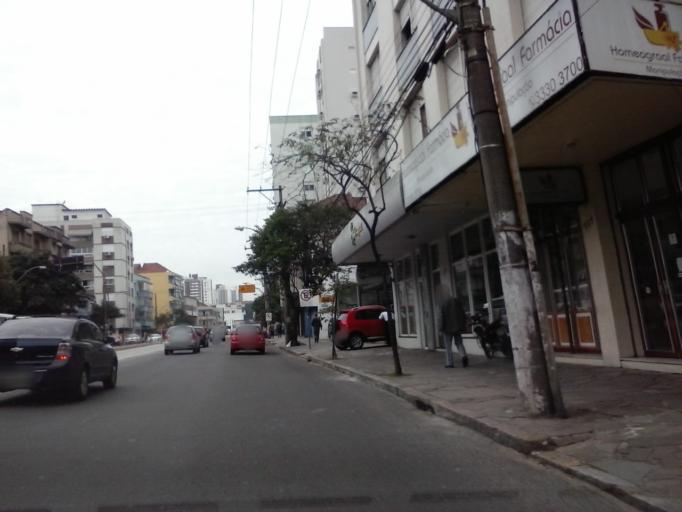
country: BR
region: Rio Grande do Sul
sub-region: Porto Alegre
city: Porto Alegre
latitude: -30.0393
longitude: -51.2005
